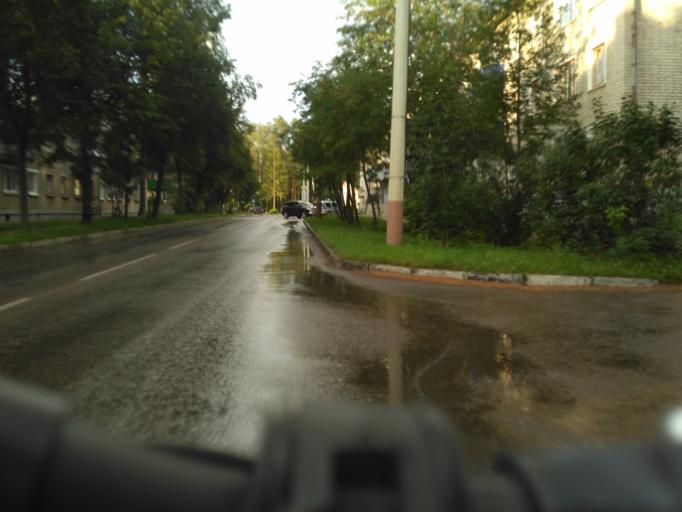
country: RU
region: Moskovskaya
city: Dubna
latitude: 56.7491
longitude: 37.2033
